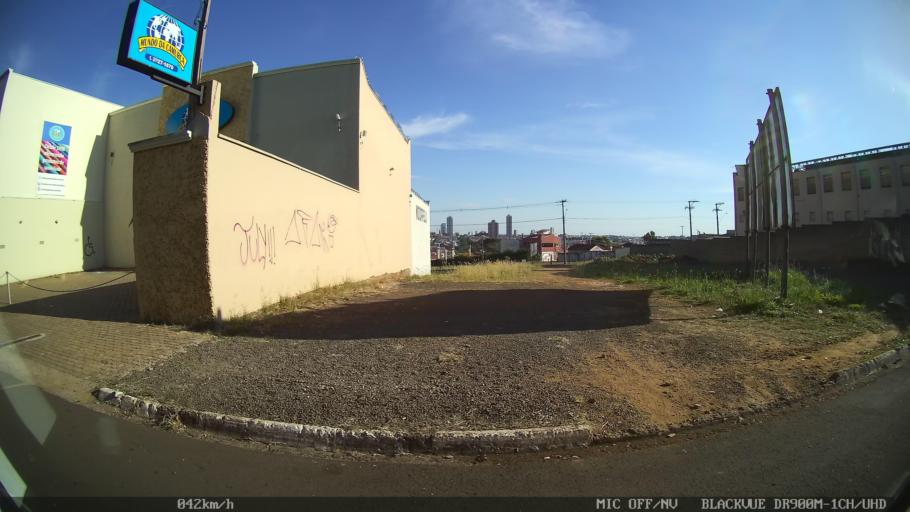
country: BR
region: Sao Paulo
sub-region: Franca
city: Franca
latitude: -20.5165
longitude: -47.3844
